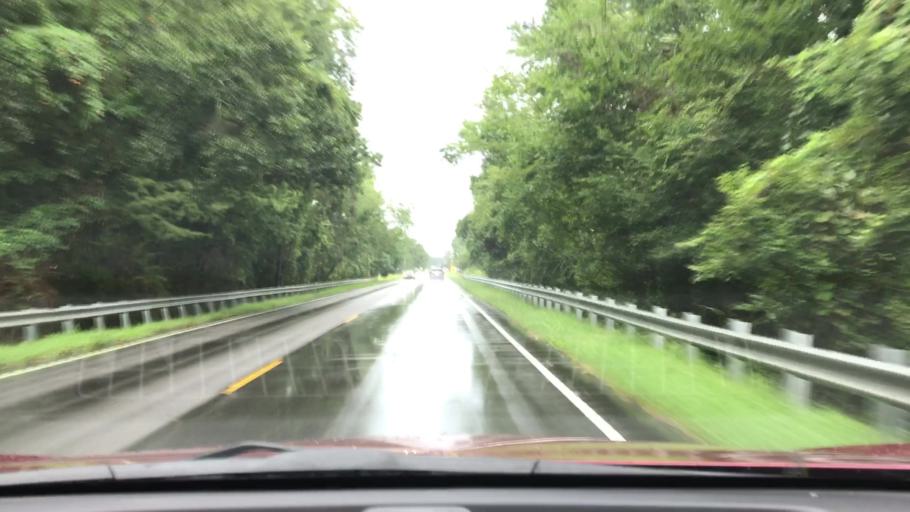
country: US
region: South Carolina
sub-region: Horry County
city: Socastee
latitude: 33.6872
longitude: -79.1211
